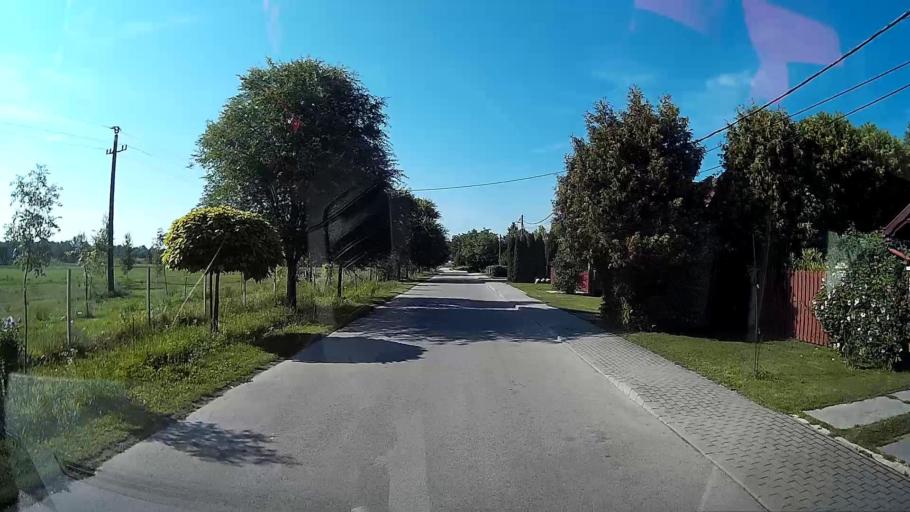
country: HU
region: Pest
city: Leanyfalu
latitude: 47.7155
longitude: 19.1003
